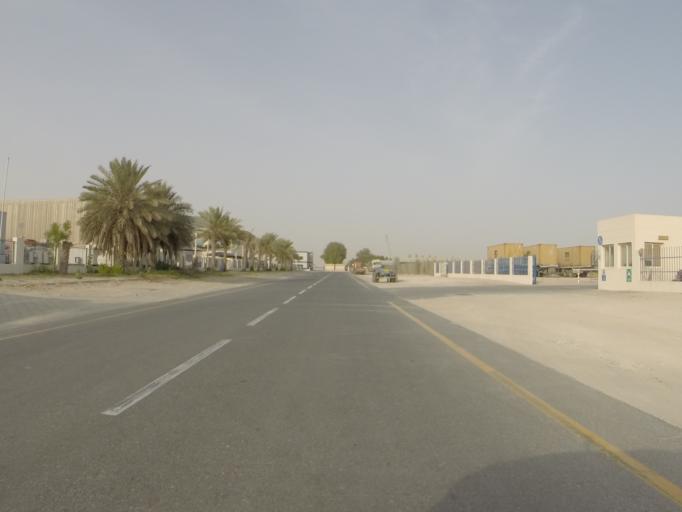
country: AE
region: Dubai
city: Dubai
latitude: 24.9534
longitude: 55.0624
